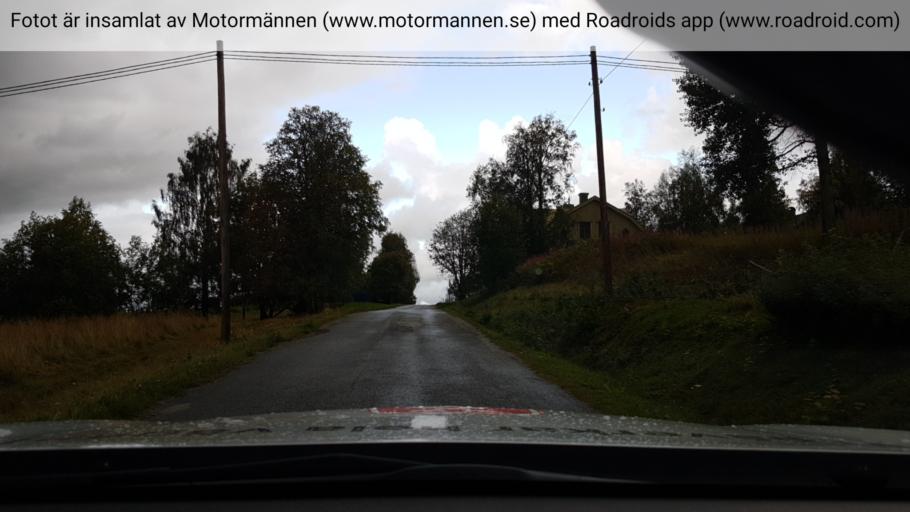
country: SE
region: Vaesterbotten
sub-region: Asele Kommun
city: Asele
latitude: 64.1883
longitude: 16.9173
